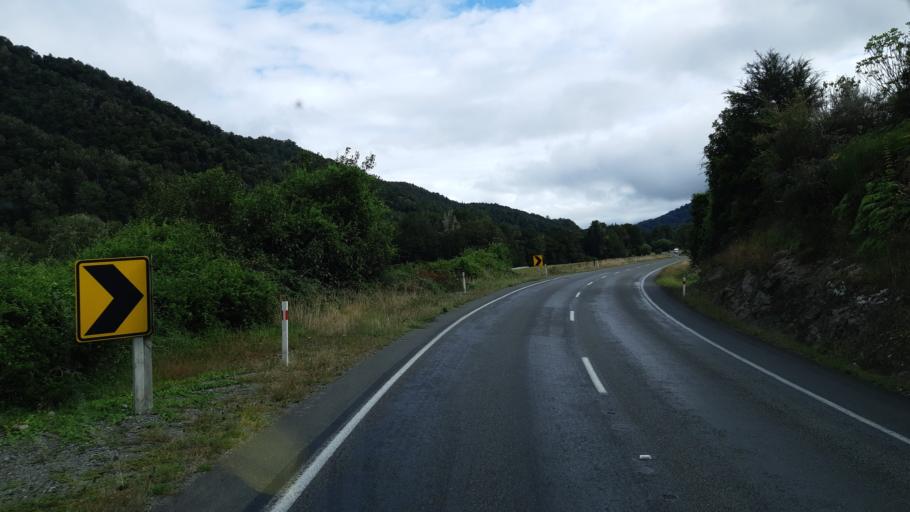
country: NZ
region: West Coast
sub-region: Buller District
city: Westport
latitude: -41.8394
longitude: 172.2429
